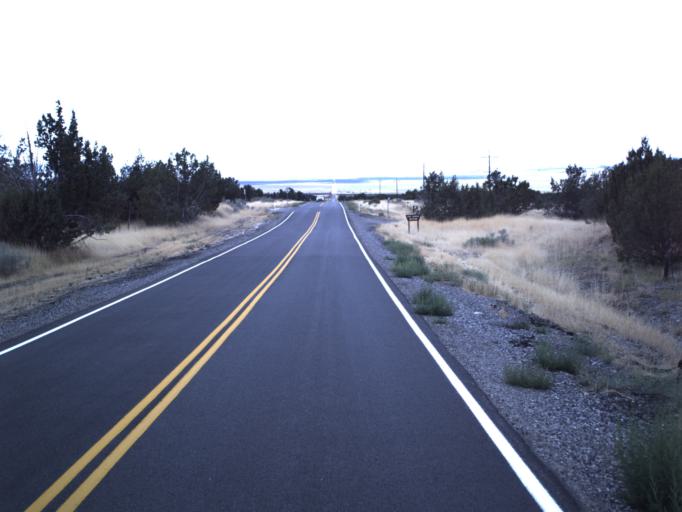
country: US
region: Utah
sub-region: Tooele County
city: Grantsville
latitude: 40.3183
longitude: -112.6295
